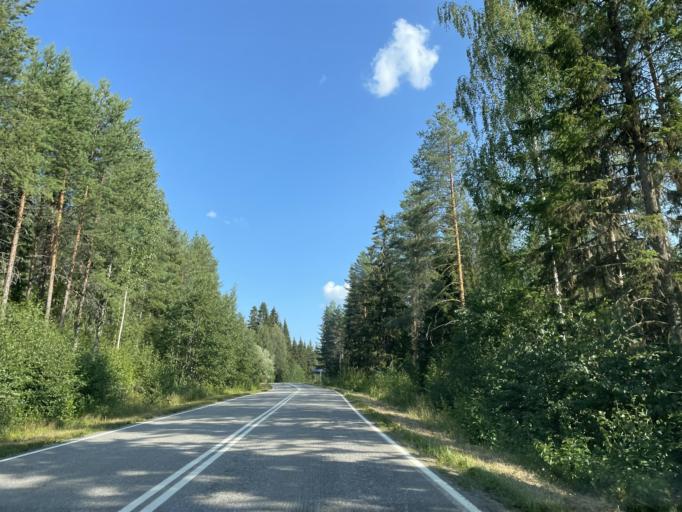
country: FI
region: Central Finland
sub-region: Saarijaervi-Viitasaari
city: Pihtipudas
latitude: 63.3646
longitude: 25.7365
